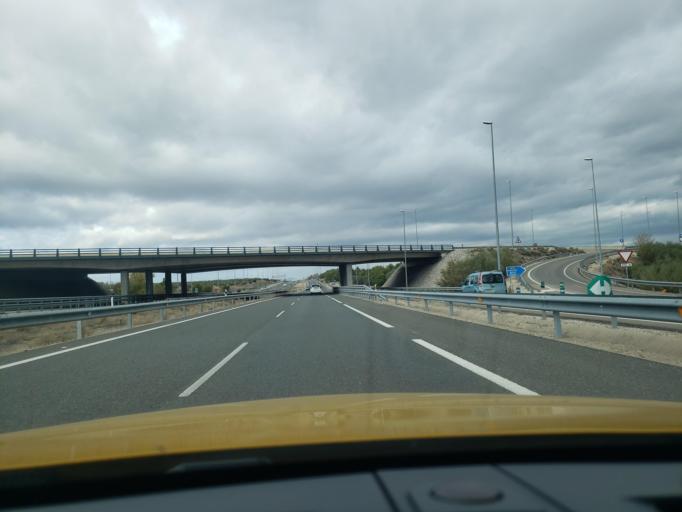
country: ES
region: Andalusia
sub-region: Provincia de Jaen
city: Jaen
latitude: 37.8167
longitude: -3.7656
